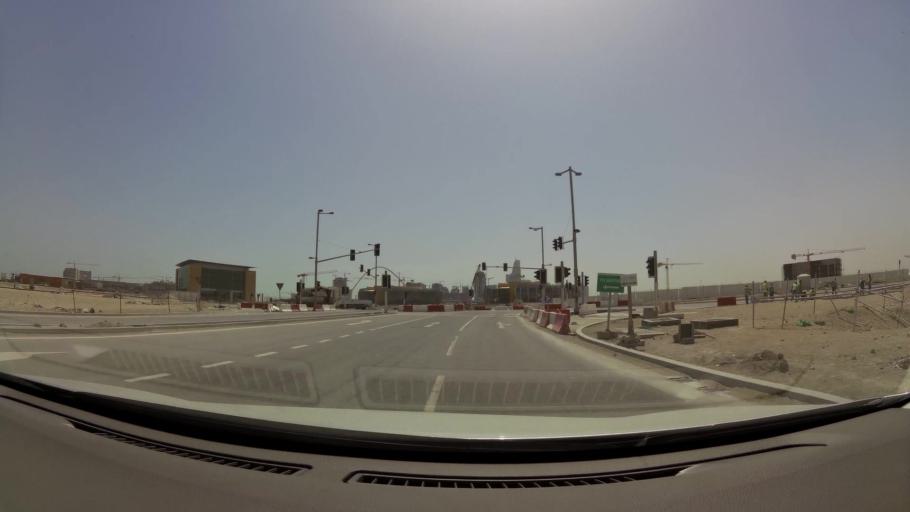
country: QA
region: Baladiyat Umm Salal
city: Umm Salal Muhammad
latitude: 25.4044
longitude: 51.5074
